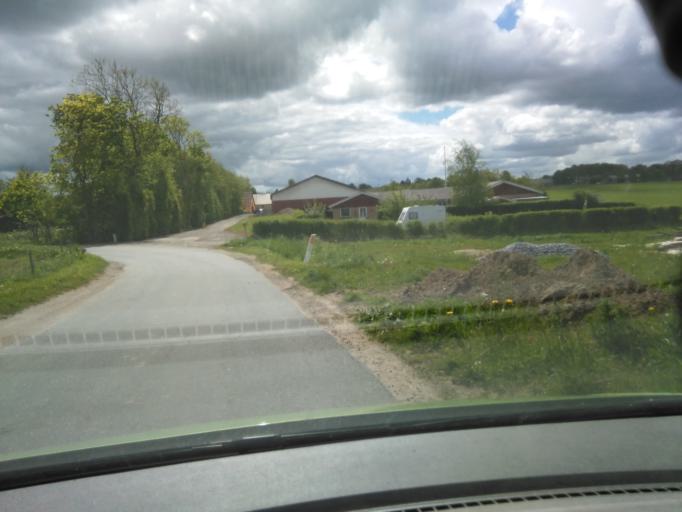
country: DK
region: Central Jutland
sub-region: Arhus Kommune
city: Tranbjerg
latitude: 56.0655
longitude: 10.1059
